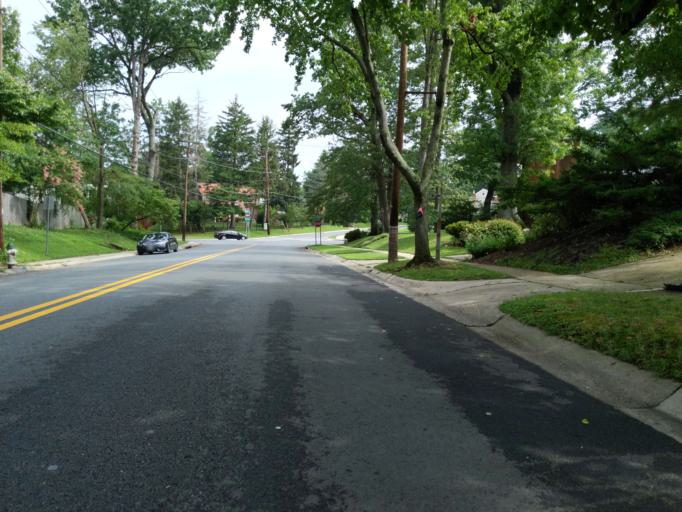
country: US
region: Maryland
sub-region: Montgomery County
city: Wheaton
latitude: 39.0291
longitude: -77.0550
